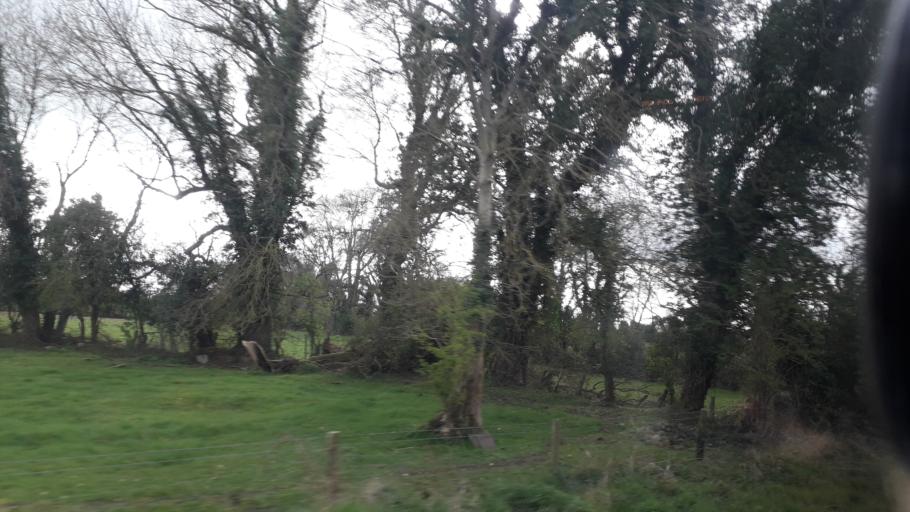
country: IE
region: Leinster
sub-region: An Iarmhi
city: Rathwire
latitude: 53.4941
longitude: -7.1612
